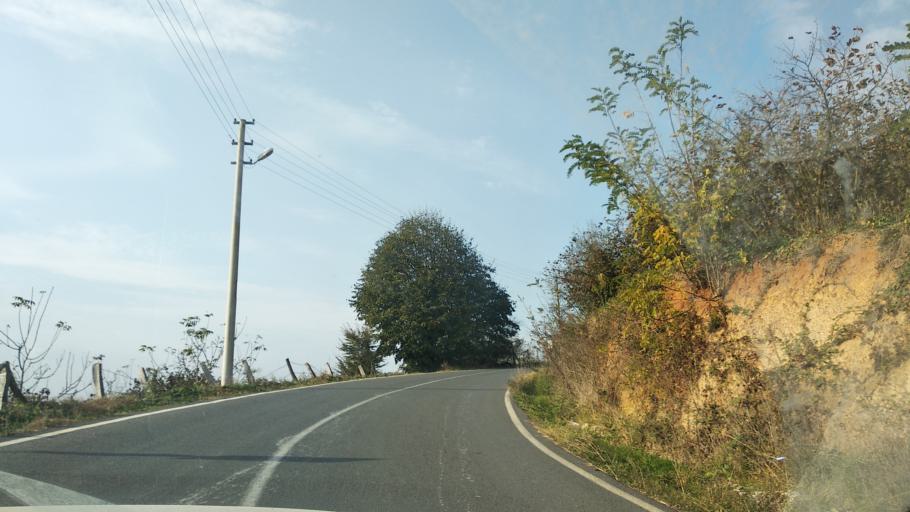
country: TR
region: Sakarya
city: Karasu
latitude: 41.0609
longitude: 30.6185
